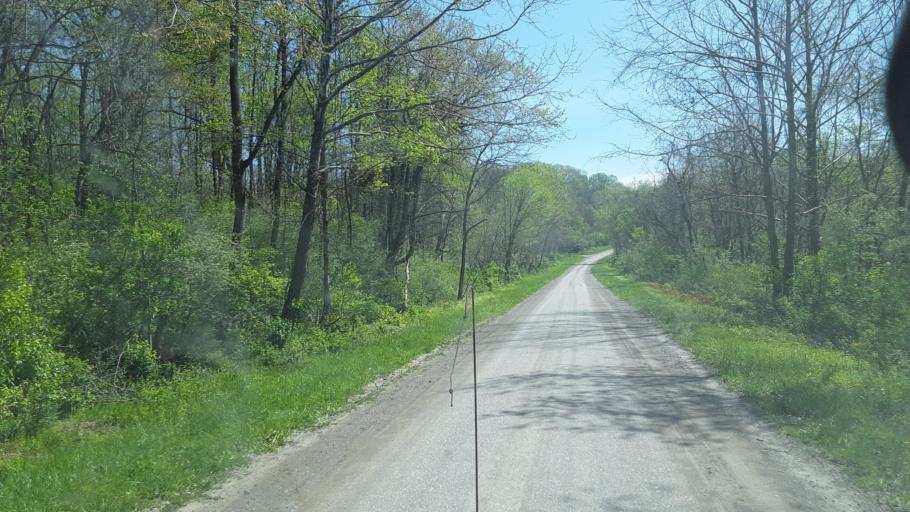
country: US
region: Ohio
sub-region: Noble County
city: Caldwell
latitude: 39.7732
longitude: -81.6257
